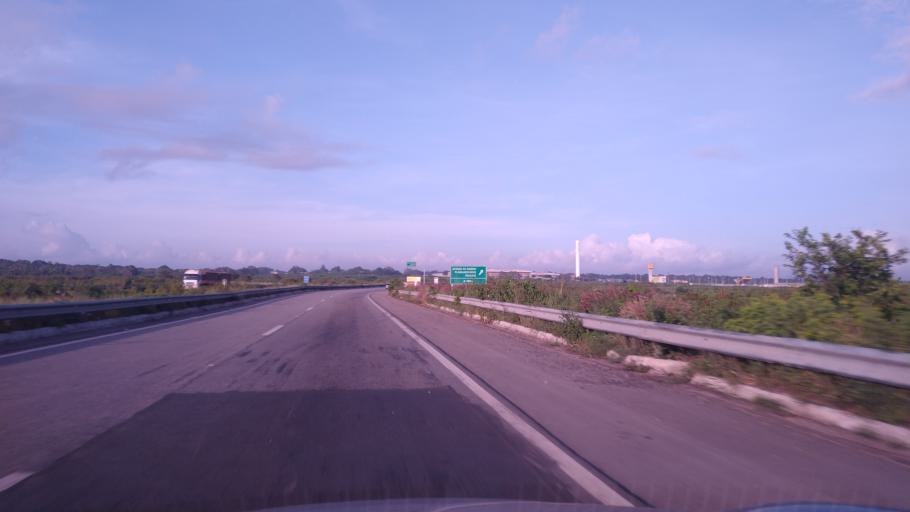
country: BR
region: Ceara
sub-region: Pacajus
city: Pacajus
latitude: -4.1594
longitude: -38.4835
